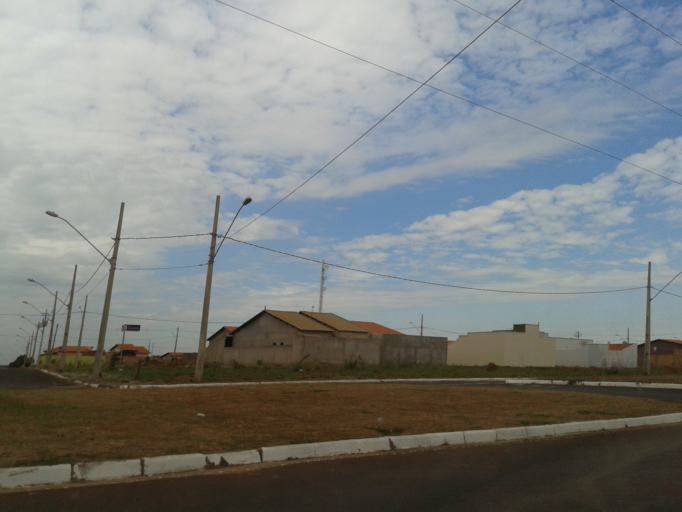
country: BR
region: Minas Gerais
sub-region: Santa Vitoria
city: Santa Vitoria
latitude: -18.8576
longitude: -50.1231
